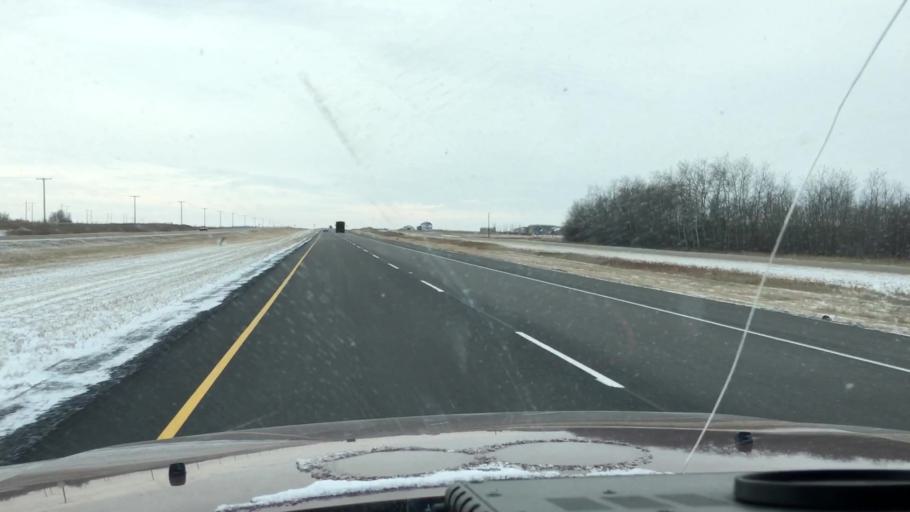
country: CA
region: Saskatchewan
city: Saskatoon
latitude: 51.9359
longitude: -106.5380
